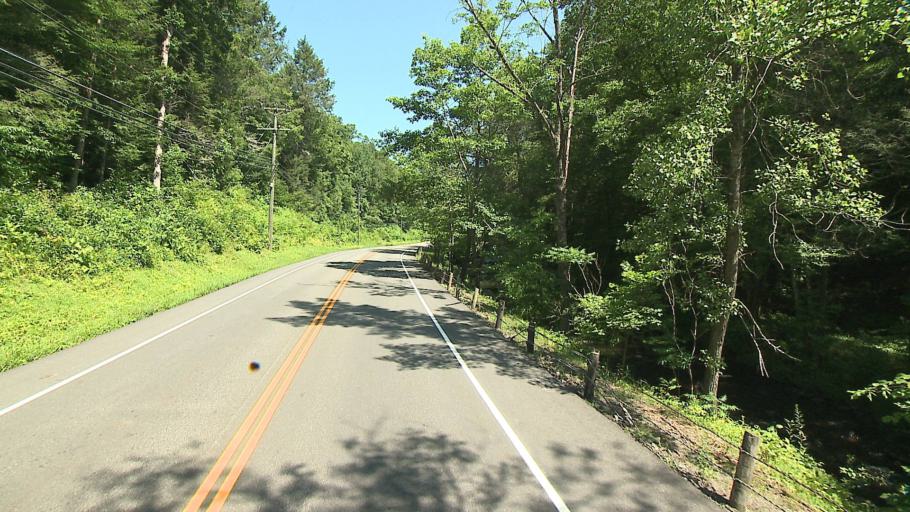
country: US
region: Connecticut
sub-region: Litchfield County
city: New Preston
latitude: 41.8230
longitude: -73.3585
